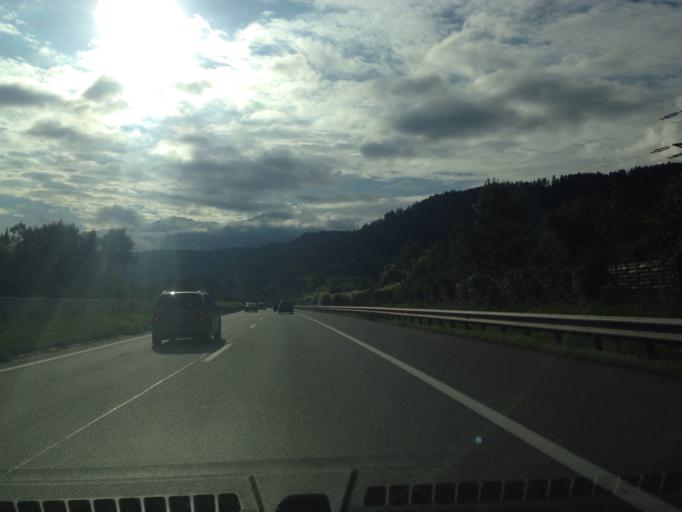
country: AT
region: Tyrol
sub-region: Politischer Bezirk Innsbruck Land
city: Vols
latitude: 47.2555
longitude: 11.3295
